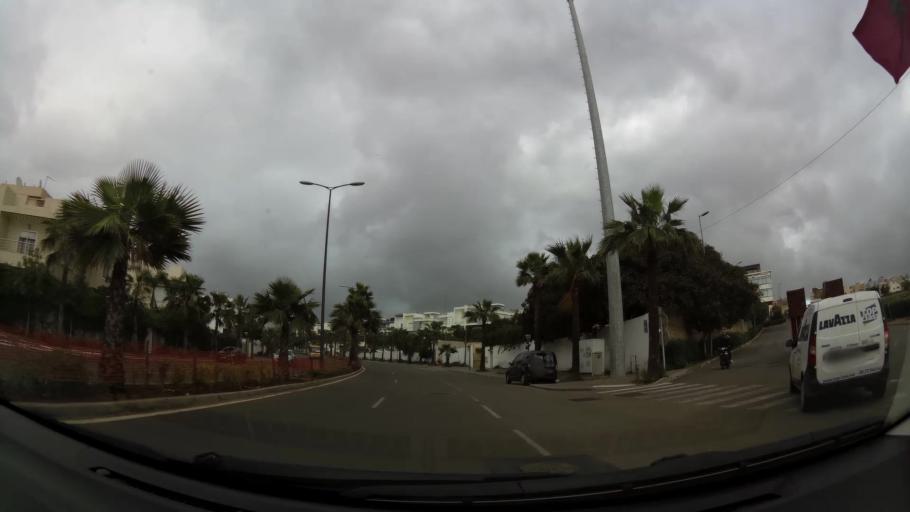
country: MA
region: Grand Casablanca
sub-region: Casablanca
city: Casablanca
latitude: 33.5702
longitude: -7.6976
